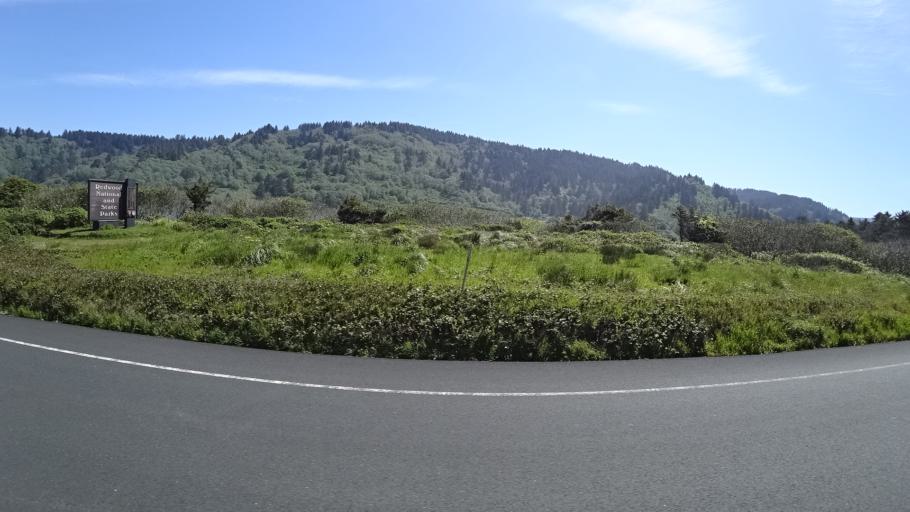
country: US
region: California
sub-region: Humboldt County
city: Westhaven-Moonstone
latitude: 41.2661
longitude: -124.0978
